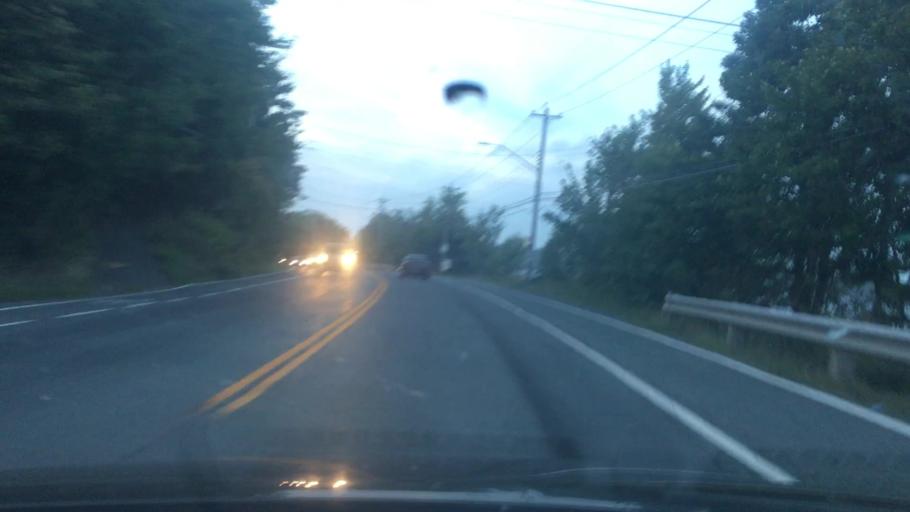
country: CA
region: Nova Scotia
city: Dartmouth
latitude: 44.6870
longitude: -63.6591
